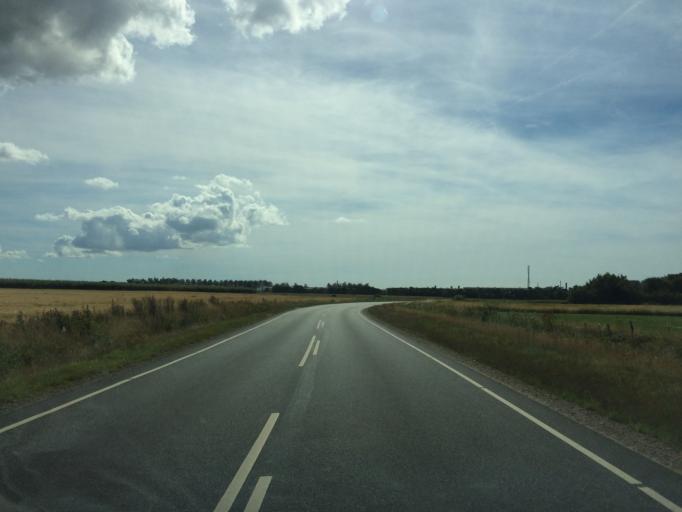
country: DK
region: Central Jutland
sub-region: Ringkobing-Skjern Kommune
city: Skjern
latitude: 56.0256
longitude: 8.3941
